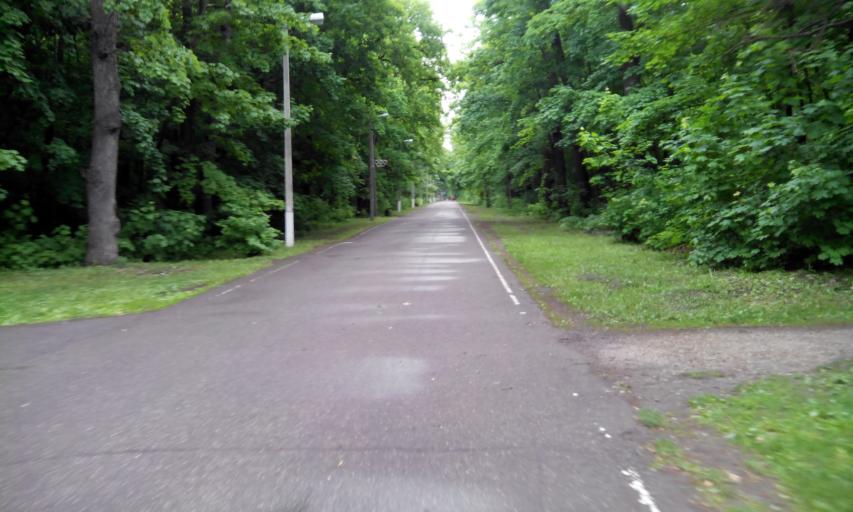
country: RU
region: Penza
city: Penza
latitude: 53.1809
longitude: 44.9721
